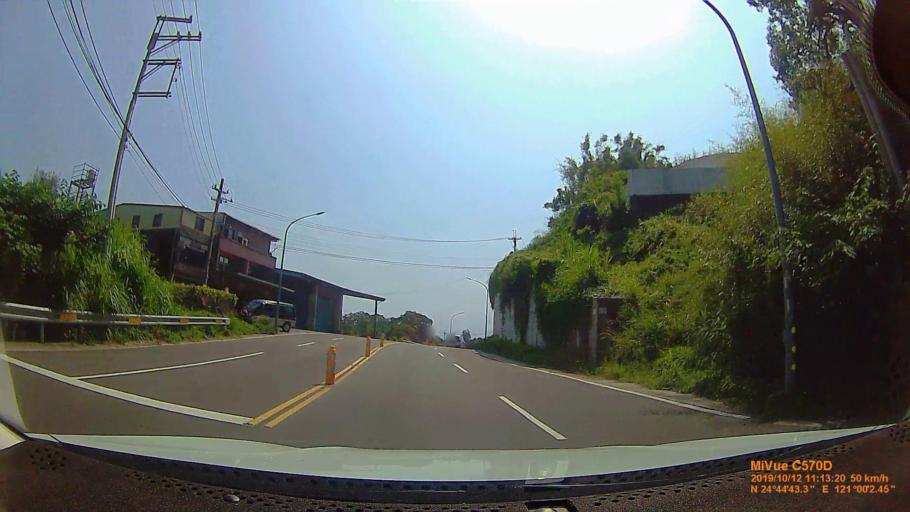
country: TW
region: Taiwan
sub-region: Hsinchu
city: Hsinchu
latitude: 24.7453
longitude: 121.0008
